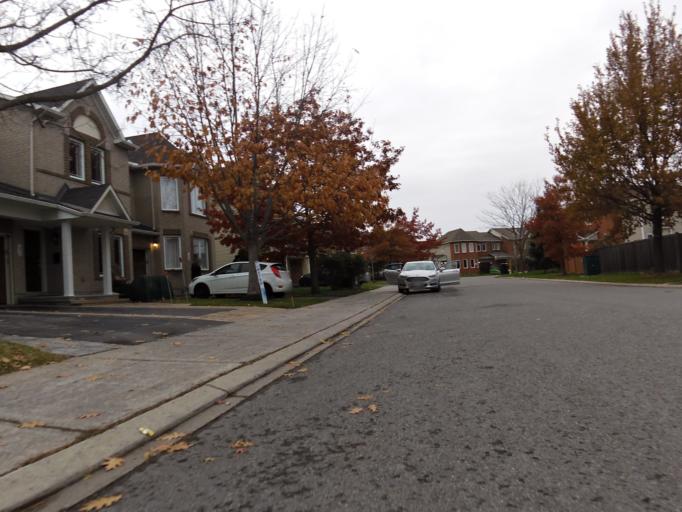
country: CA
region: Ontario
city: Bells Corners
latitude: 45.2732
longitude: -75.7067
